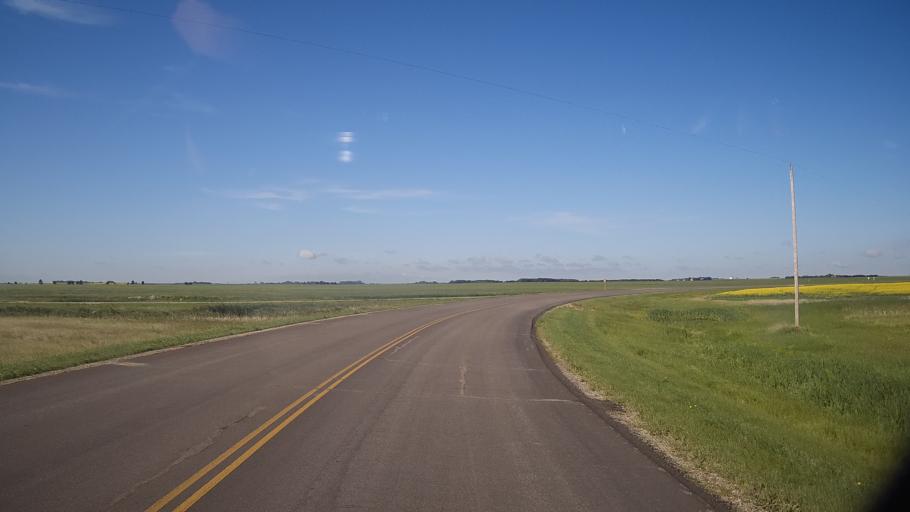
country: CA
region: Saskatchewan
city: Watrous
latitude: 51.6793
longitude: -105.3820
